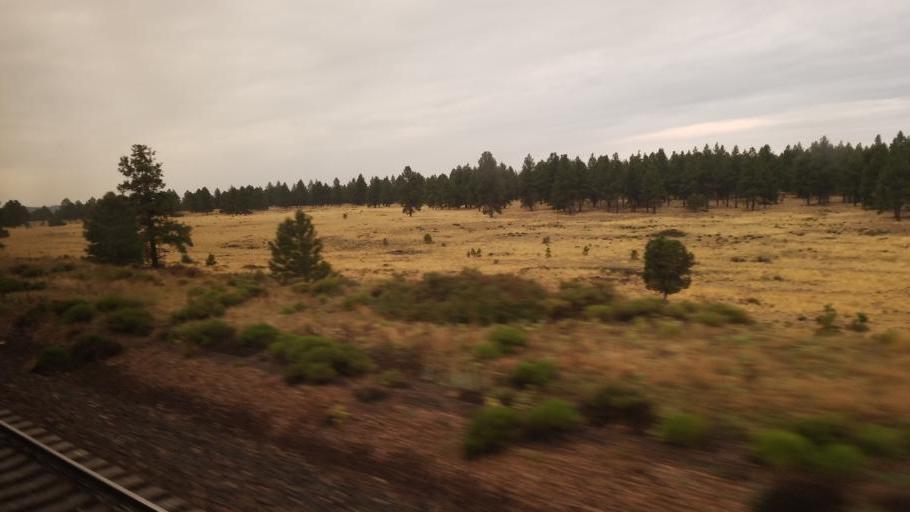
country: US
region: Arizona
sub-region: Coconino County
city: Parks
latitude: 35.2406
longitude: -111.9845
